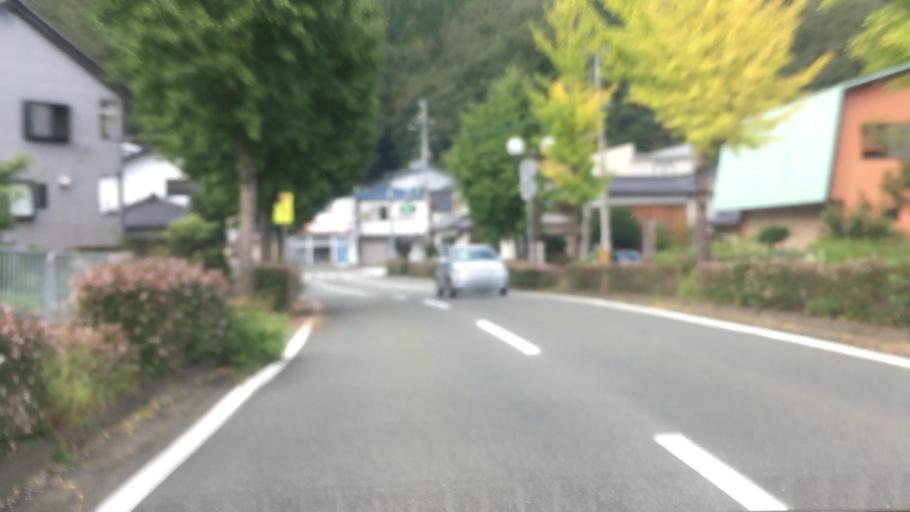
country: JP
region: Hyogo
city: Toyooka
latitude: 35.4050
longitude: 134.7646
